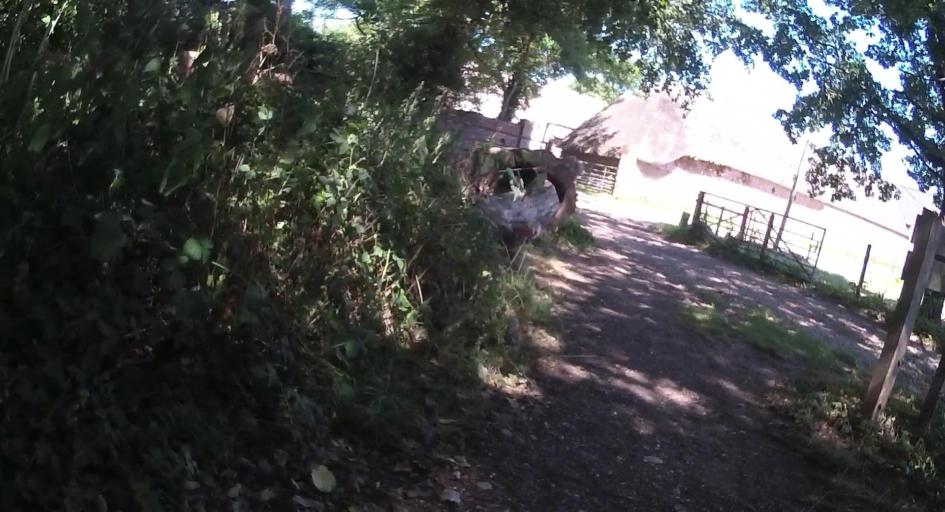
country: GB
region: England
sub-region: Dorset
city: Bovington Camp
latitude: 50.7402
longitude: -2.2423
